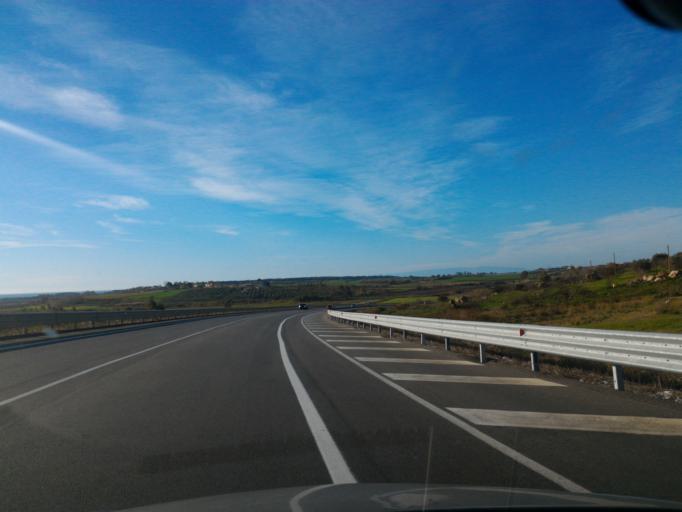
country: IT
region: Calabria
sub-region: Provincia di Crotone
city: Isola di Capo Rizzuto
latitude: 38.9421
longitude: 17.0800
